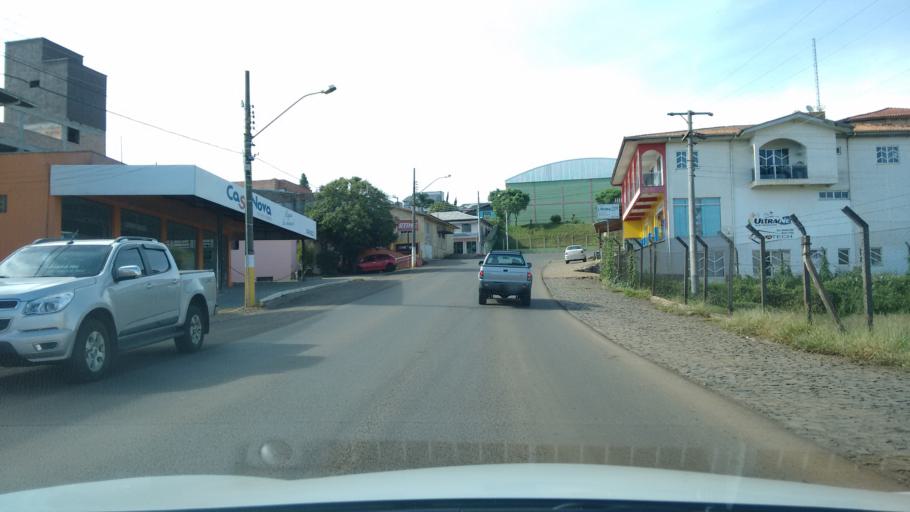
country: BR
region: Santa Catarina
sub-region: Videira
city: Videira
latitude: -27.2231
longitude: -50.9785
